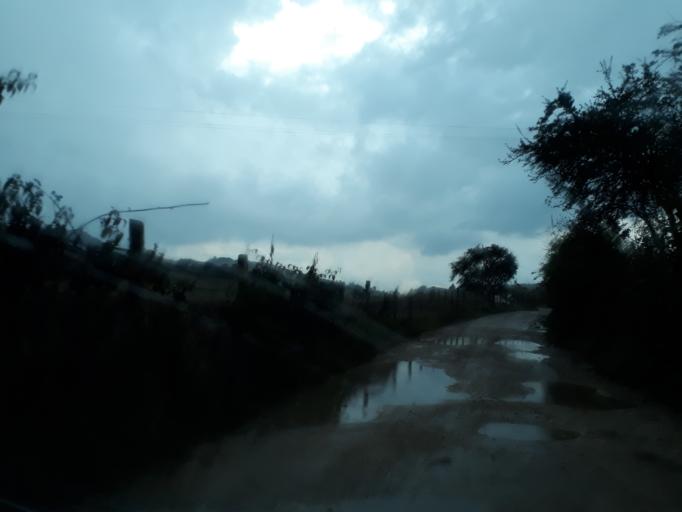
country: CO
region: Cundinamarca
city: Villapinzon
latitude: 5.3005
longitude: -73.6006
